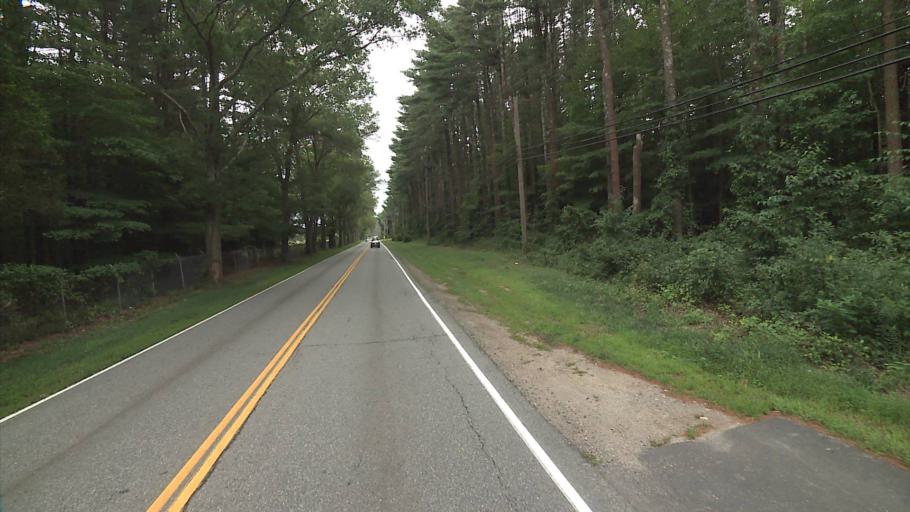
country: US
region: Connecticut
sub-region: New London County
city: Oxoboxo River
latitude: 41.4094
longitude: -72.1840
